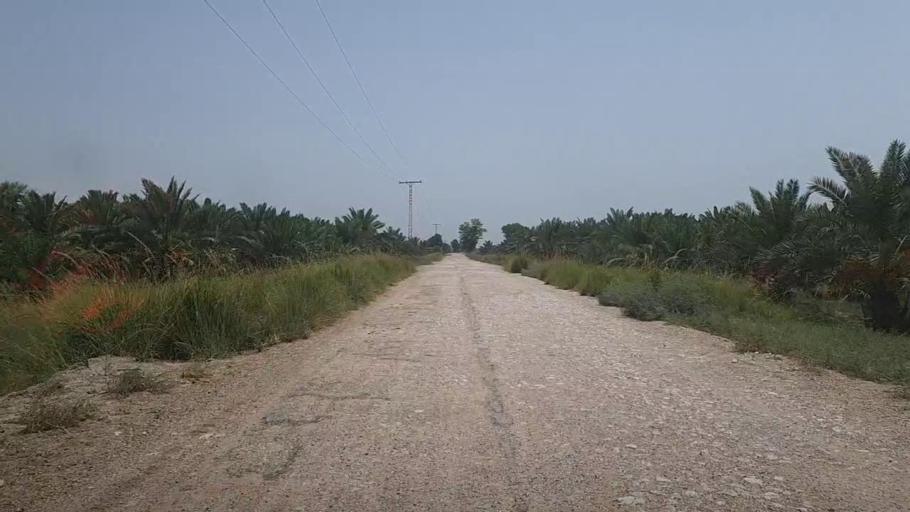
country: PK
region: Sindh
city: Pad Idan
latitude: 26.8479
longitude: 68.3248
